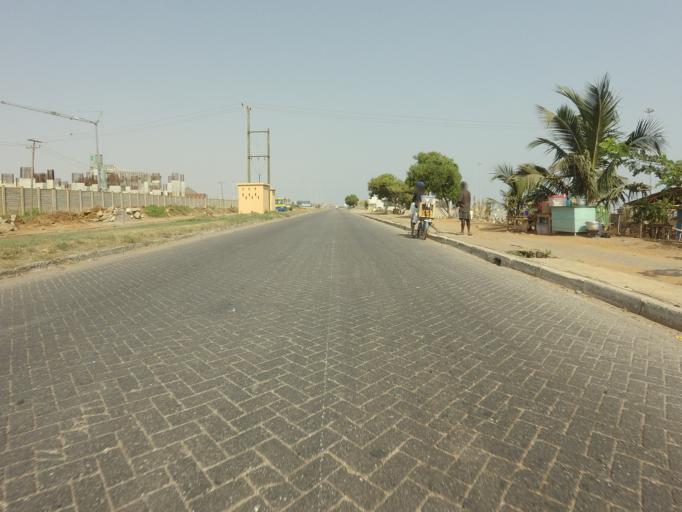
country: GH
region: Greater Accra
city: Tema
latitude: 5.6194
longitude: -0.0160
